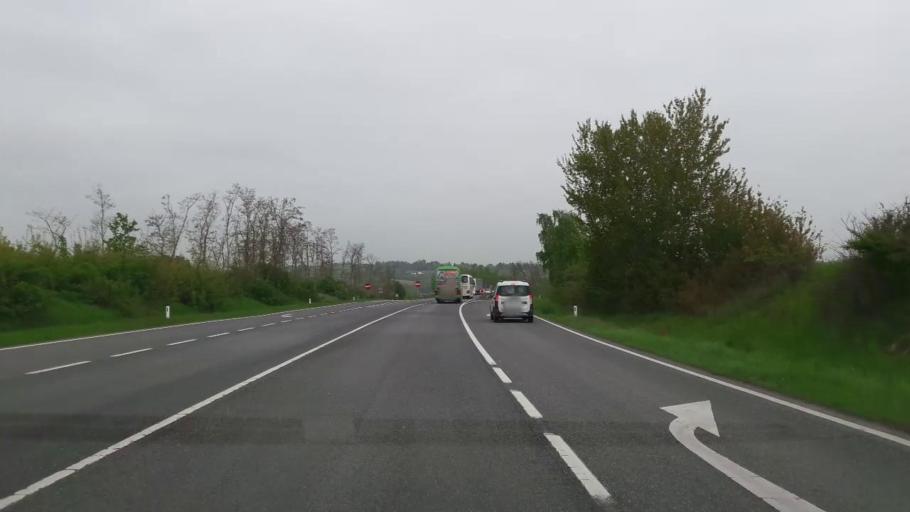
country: AT
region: Lower Austria
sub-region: Politischer Bezirk Hollabrunn
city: Hollabrunn
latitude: 48.5528
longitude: 16.0670
